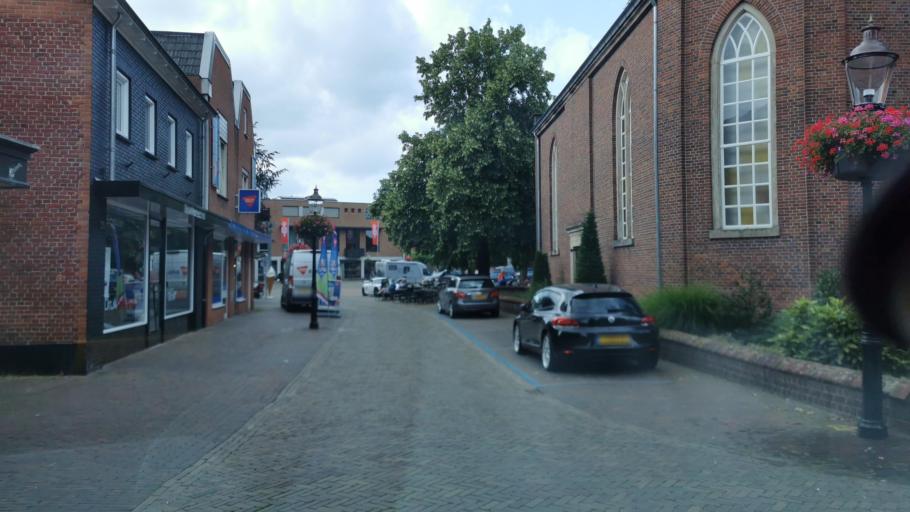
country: NL
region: Overijssel
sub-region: Gemeente Losser
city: Losser
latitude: 52.2622
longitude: 7.0071
